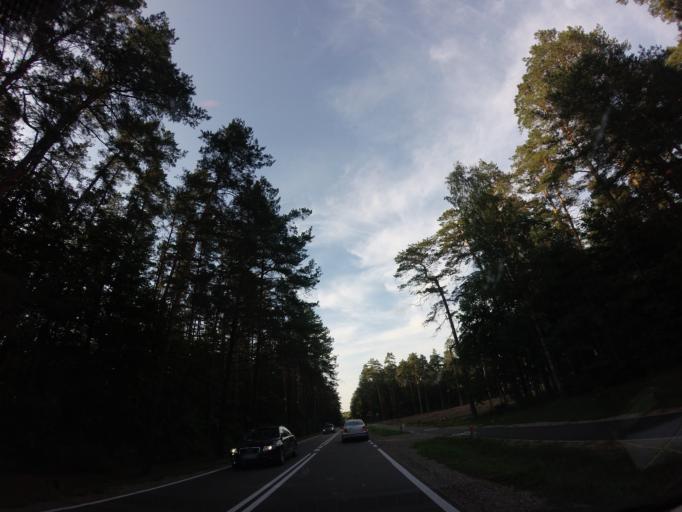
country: PL
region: Podlasie
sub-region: Powiat augustowski
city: Augustow
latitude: 53.8632
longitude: 23.0889
